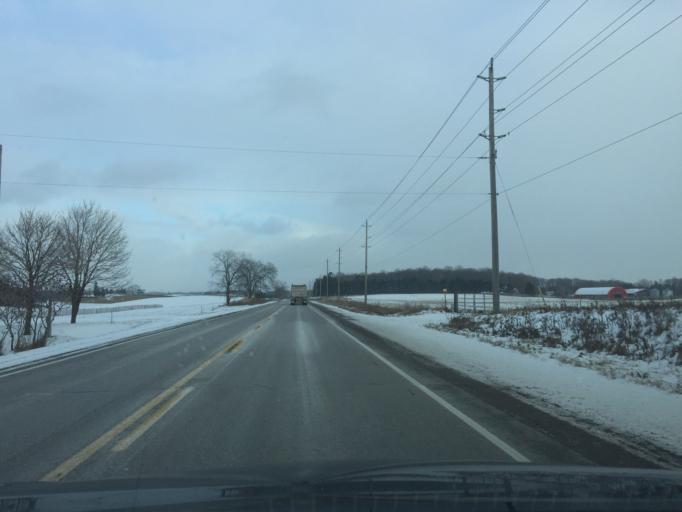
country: CA
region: Ontario
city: Uxbridge
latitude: 44.0377
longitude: -79.1806
